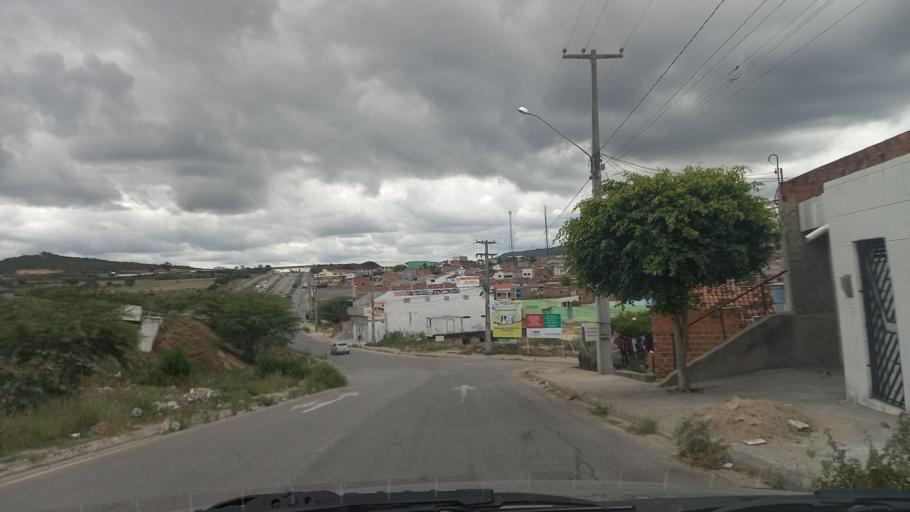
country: BR
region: Pernambuco
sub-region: Caruaru
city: Caruaru
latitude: -8.3330
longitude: -36.1383
